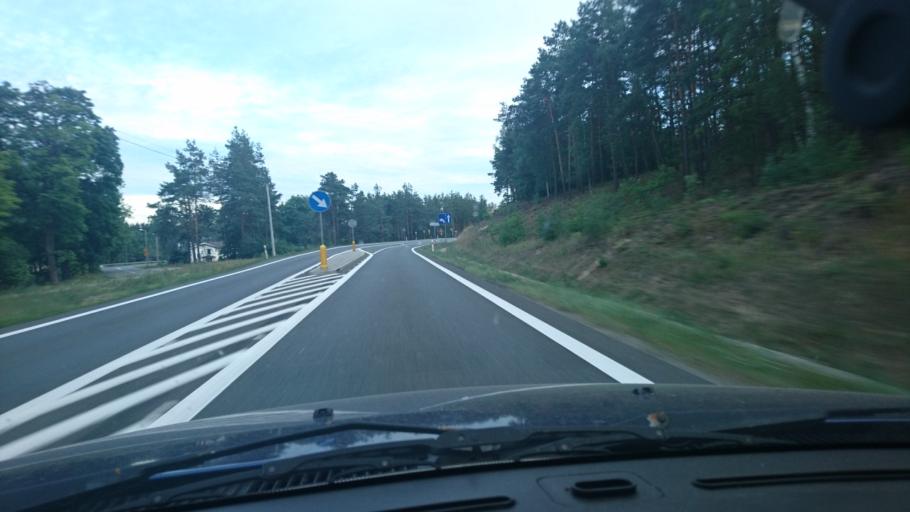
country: PL
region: Silesian Voivodeship
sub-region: Powiat tarnogorski
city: Tworog
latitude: 50.5988
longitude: 18.7024
